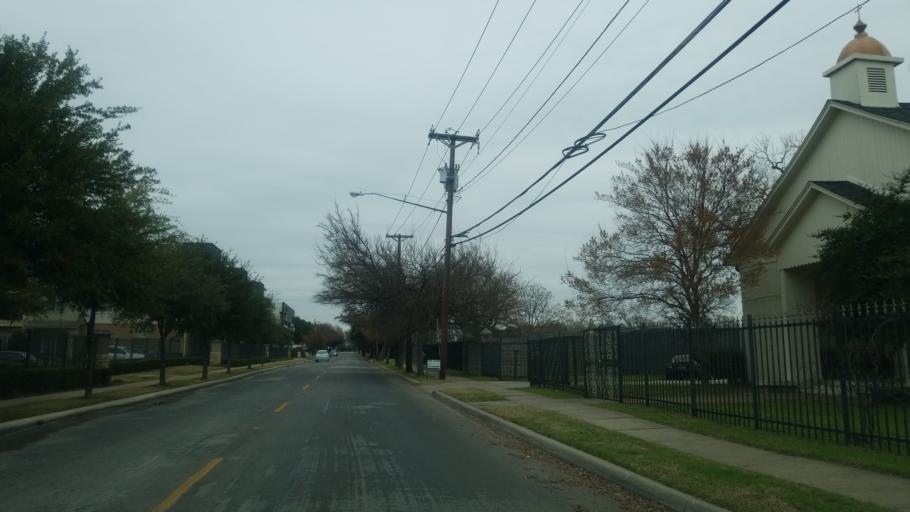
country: US
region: Texas
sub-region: Dallas County
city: Dallas
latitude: 32.8146
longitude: -96.8241
